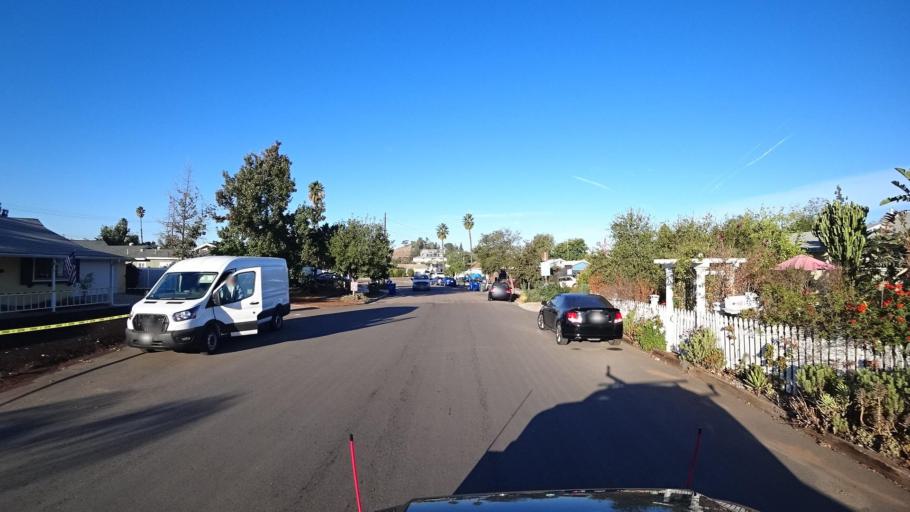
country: US
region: California
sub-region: San Diego County
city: Bostonia
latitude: 32.8174
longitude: -116.9472
